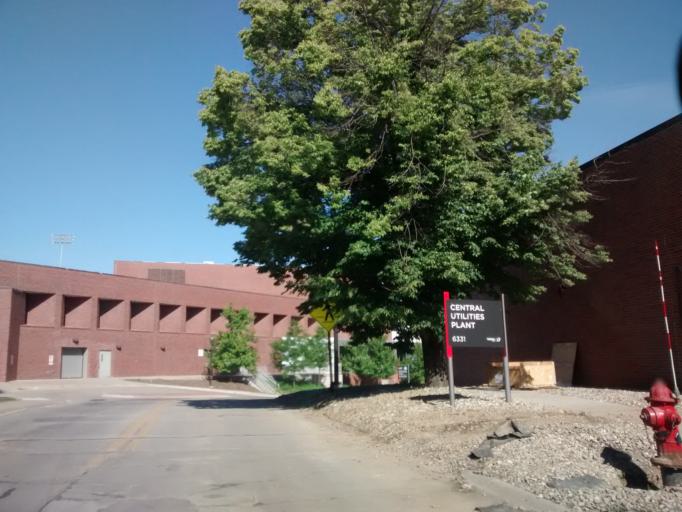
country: US
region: Nebraska
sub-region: Douglas County
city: Ralston
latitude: 41.2564
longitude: -96.0103
